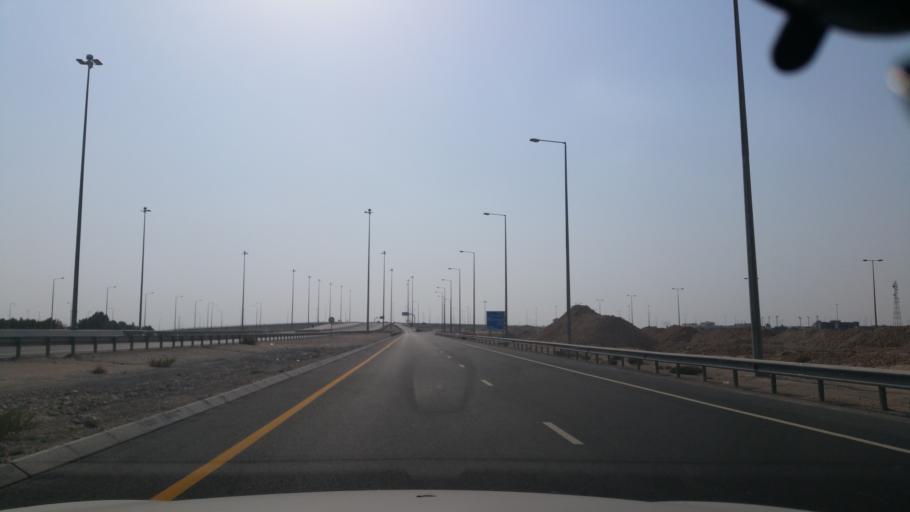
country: QA
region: Baladiyat Umm Salal
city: Umm Salal `Ali
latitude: 25.4505
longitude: 51.4173
